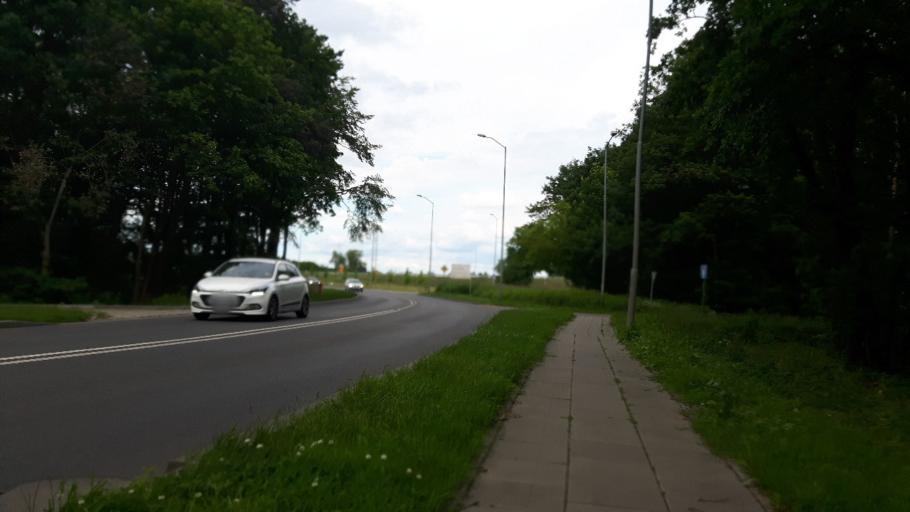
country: PL
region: West Pomeranian Voivodeship
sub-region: Szczecin
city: Szczecin
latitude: 53.4070
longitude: 14.6973
